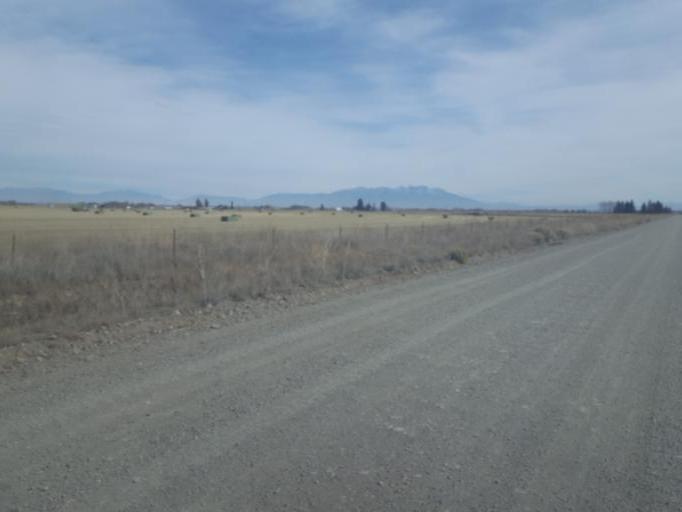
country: US
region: Colorado
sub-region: Rio Grande County
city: Monte Vista
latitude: 37.4011
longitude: -106.0864
